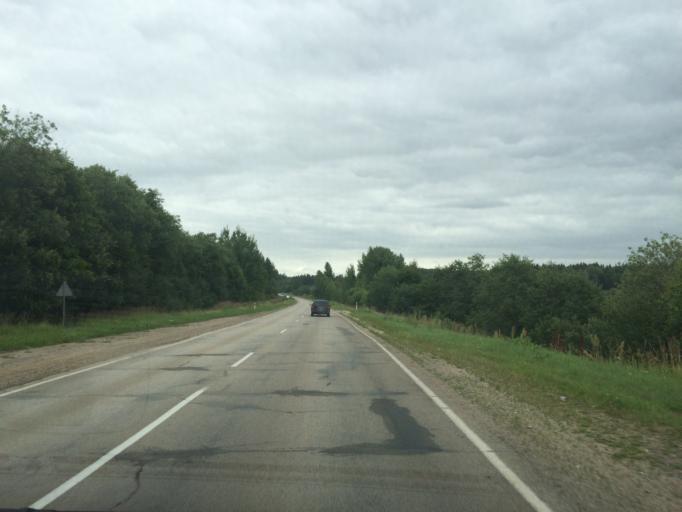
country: LV
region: Rezekne
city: Rezekne
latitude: 56.5871
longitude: 27.4033
